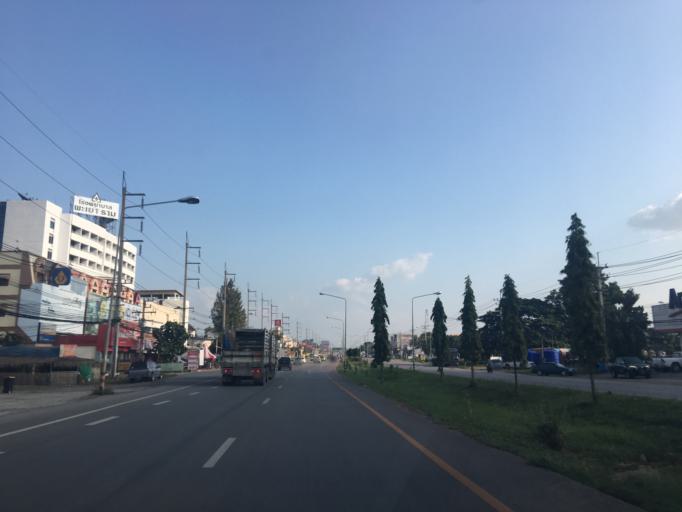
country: TH
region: Phayao
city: Phayao
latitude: 19.1790
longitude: 99.9001
